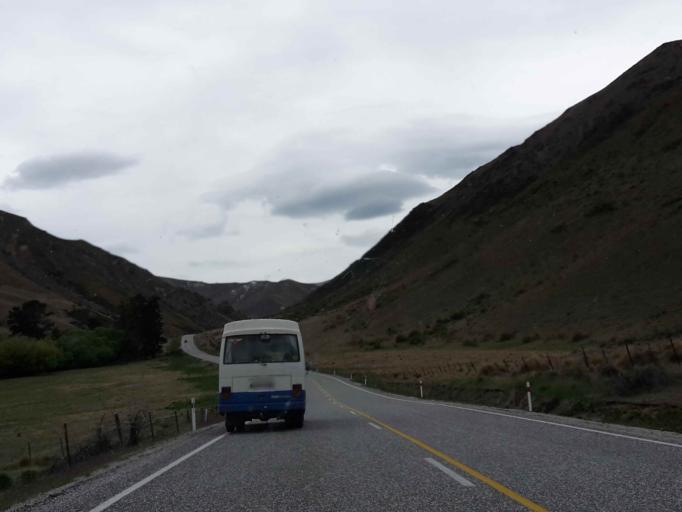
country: NZ
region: Otago
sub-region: Queenstown-Lakes District
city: Wanaka
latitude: -44.5848
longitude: 169.5861
